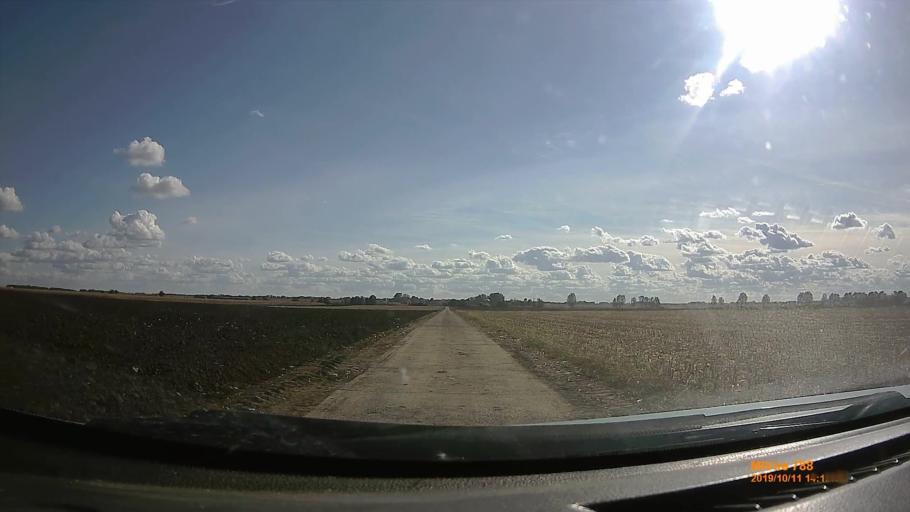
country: HU
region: Hajdu-Bihar
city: Hajduszoboszlo
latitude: 47.5367
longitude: 21.4013
